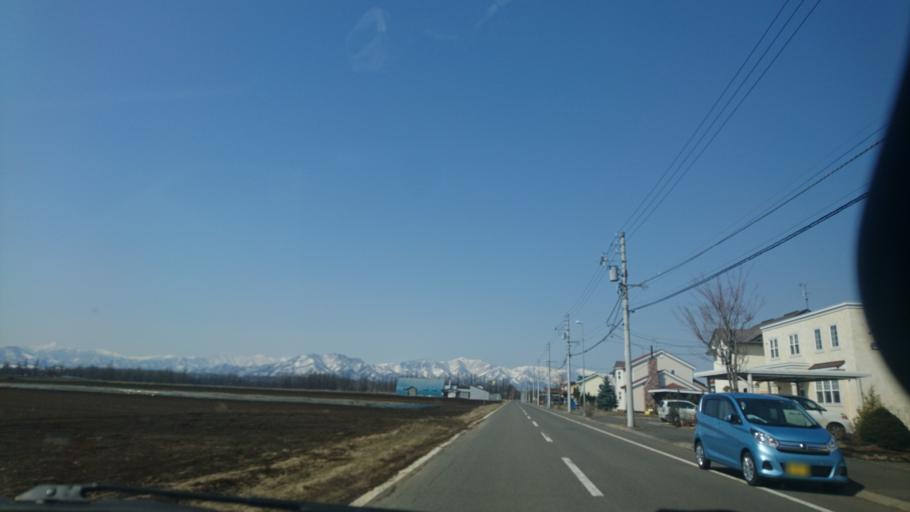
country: JP
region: Hokkaido
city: Obihiro
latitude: 42.9103
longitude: 143.0764
